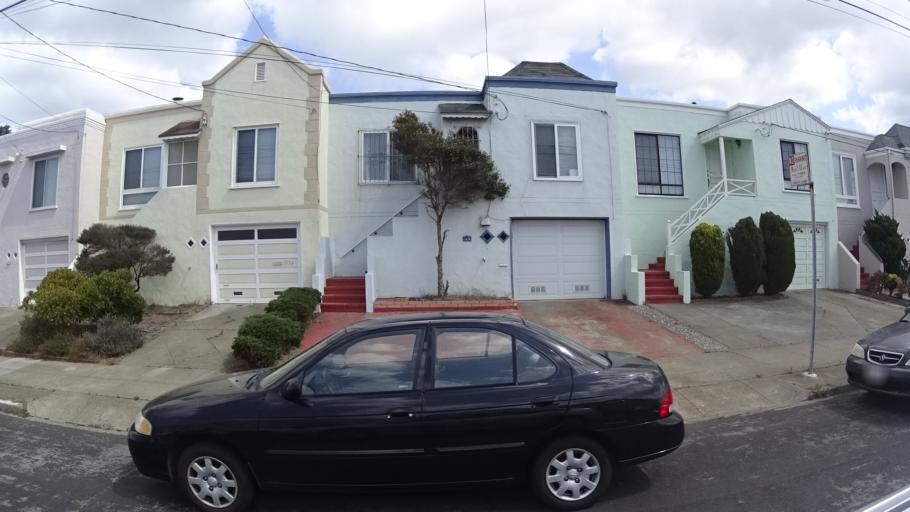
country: US
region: California
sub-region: San Mateo County
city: Daly City
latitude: 37.7501
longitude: -122.4923
